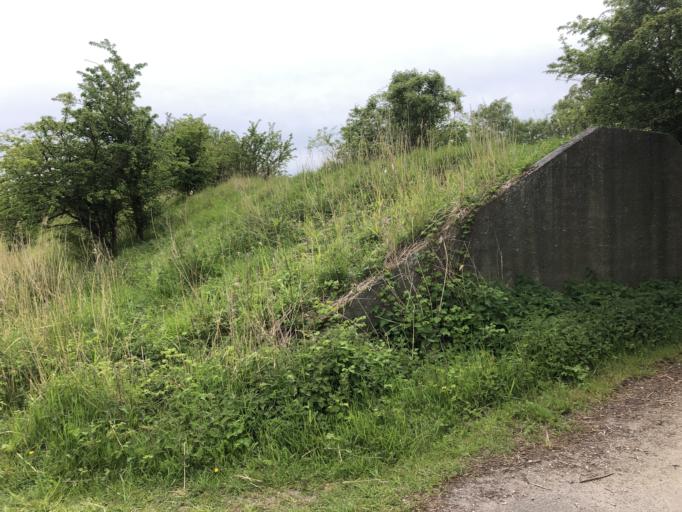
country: DK
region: Capital Region
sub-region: Tarnby Kommune
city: Tarnby
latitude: 55.5767
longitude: 12.5557
